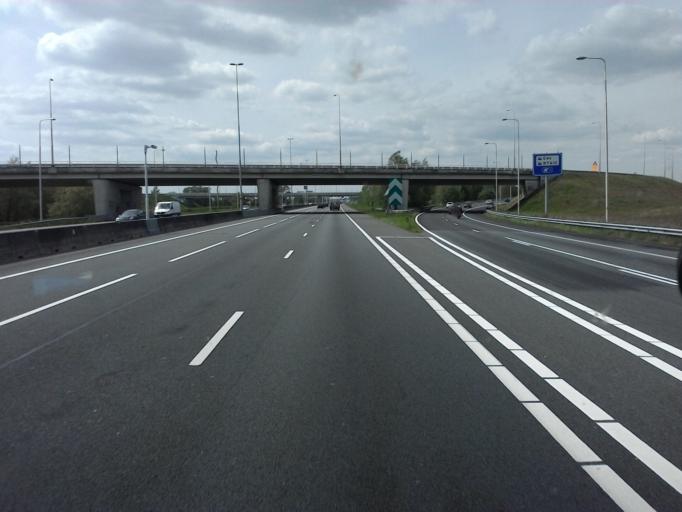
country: NL
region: Gelderland
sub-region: Gemeente Ede
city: Ede
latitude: 52.0247
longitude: 5.6151
